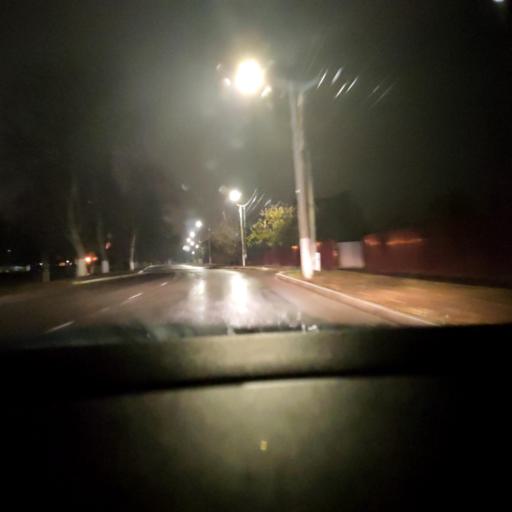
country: RU
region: Voronezj
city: Semiluki
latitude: 51.6903
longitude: 39.0370
